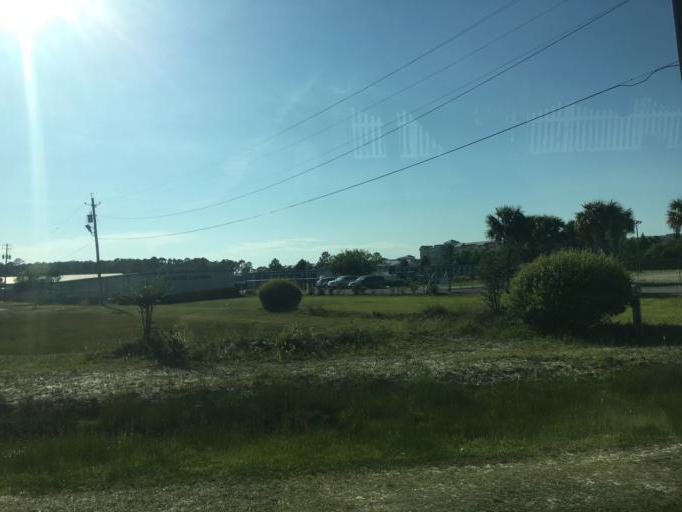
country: US
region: Florida
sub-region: Bay County
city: Panama City Beach
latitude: 30.1952
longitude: -85.8241
